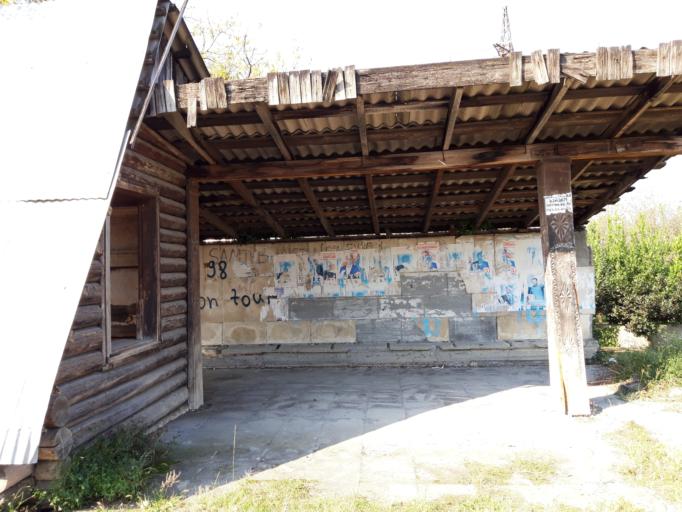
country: GE
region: Imereti
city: Samtredia
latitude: 42.1616
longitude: 42.3268
